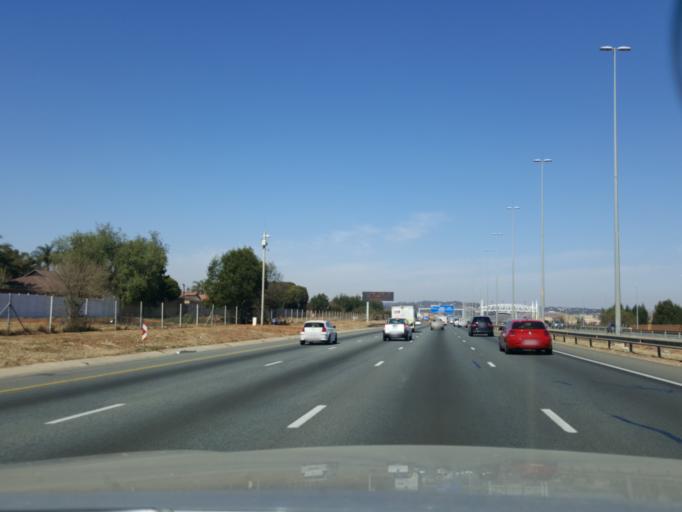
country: ZA
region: Gauteng
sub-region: City of Tshwane Metropolitan Municipality
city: Centurion
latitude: -25.8480
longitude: 28.2509
